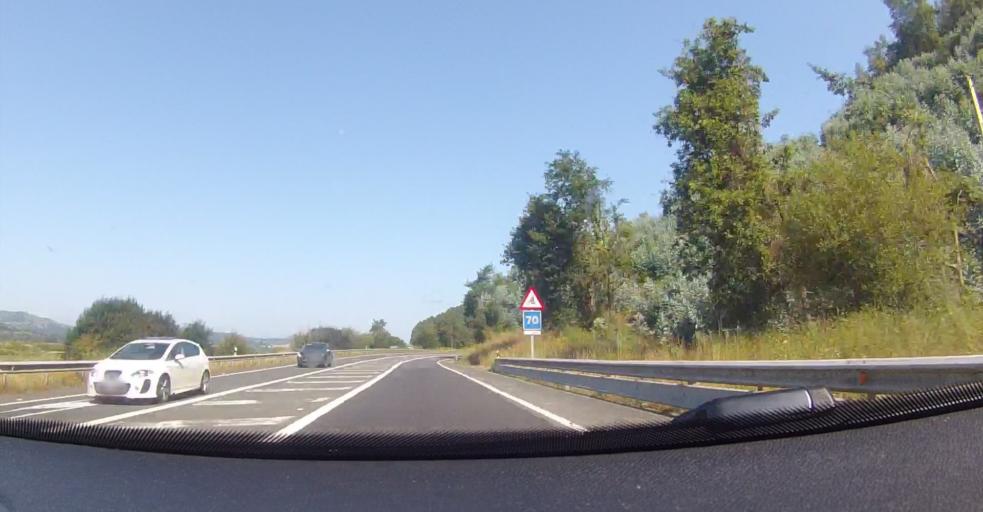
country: ES
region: Cantabria
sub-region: Provincia de Cantabria
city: Limpias
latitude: 43.3772
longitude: -3.4316
